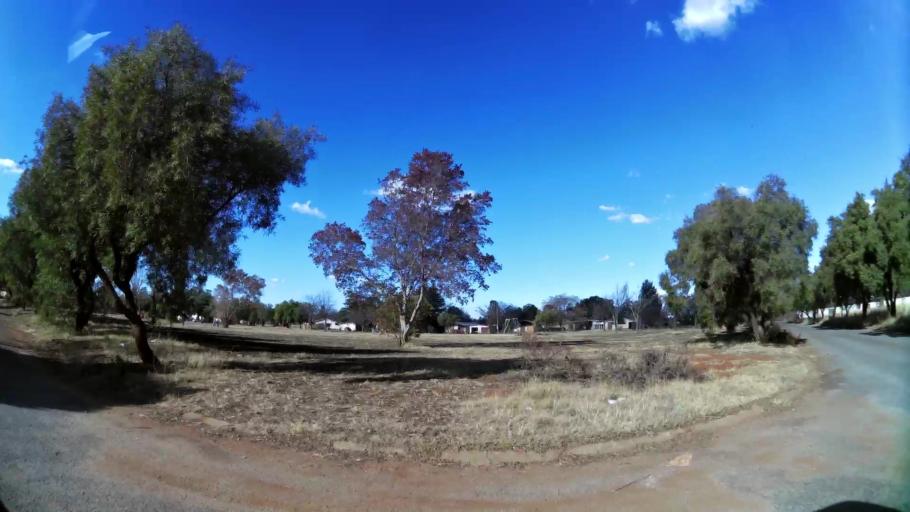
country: ZA
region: Gauteng
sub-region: West Rand District Municipality
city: Carletonville
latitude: -26.3543
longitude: 27.4130
